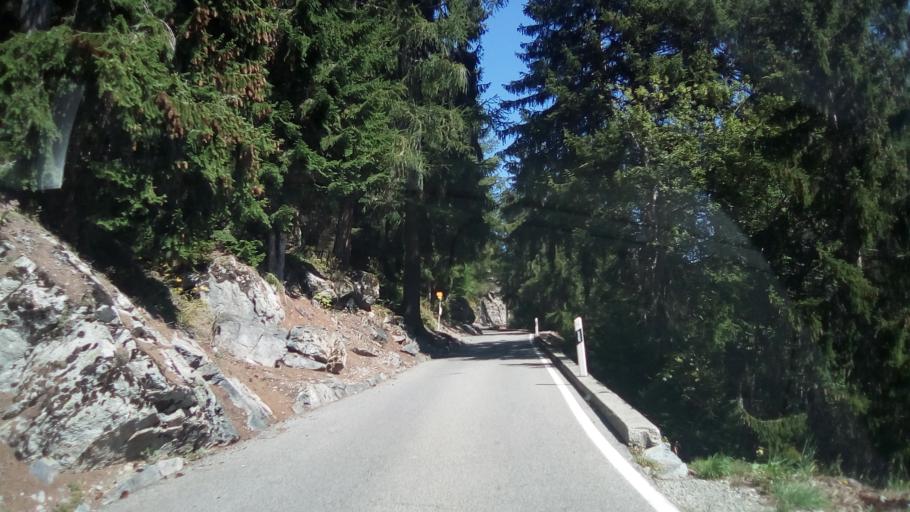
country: CH
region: Valais
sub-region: Saint-Maurice District
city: Salvan
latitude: 46.1354
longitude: 7.0186
